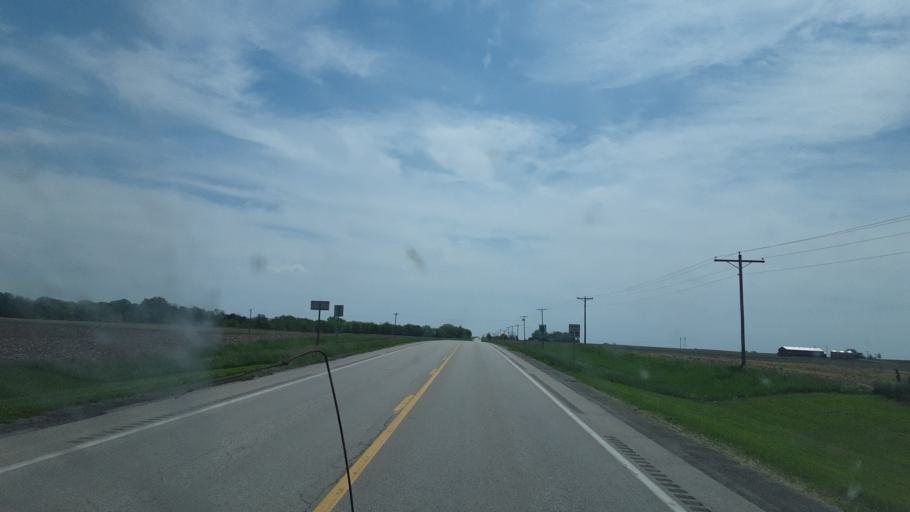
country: US
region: Illinois
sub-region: McLean County
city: Heyworth
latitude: 40.3121
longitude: -88.9647
